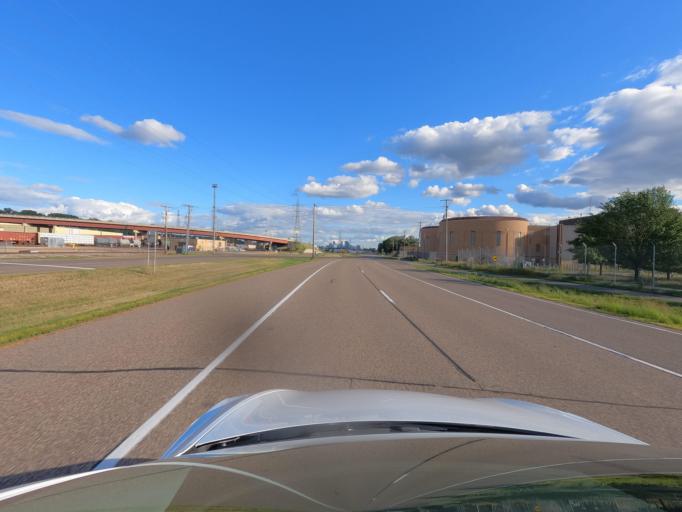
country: US
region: Minnesota
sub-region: Anoka County
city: Columbia Heights
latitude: 45.0469
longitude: -93.2750
